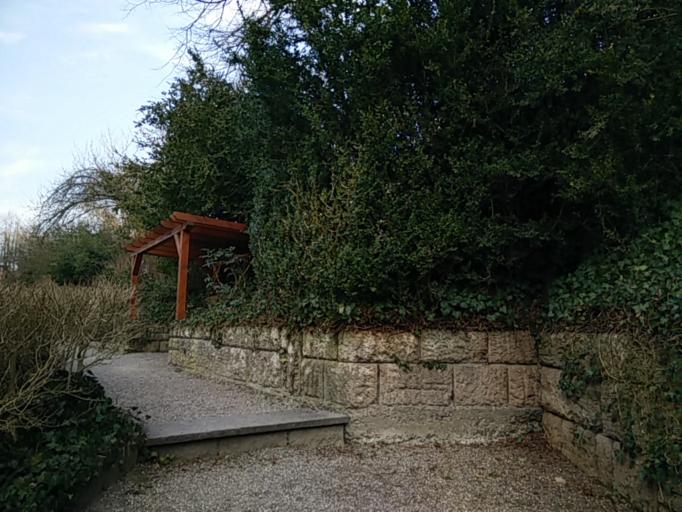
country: DE
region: Baden-Wuerttemberg
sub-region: Freiburg Region
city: Radolfzell am Bodensee
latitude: 47.7369
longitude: 8.9719
